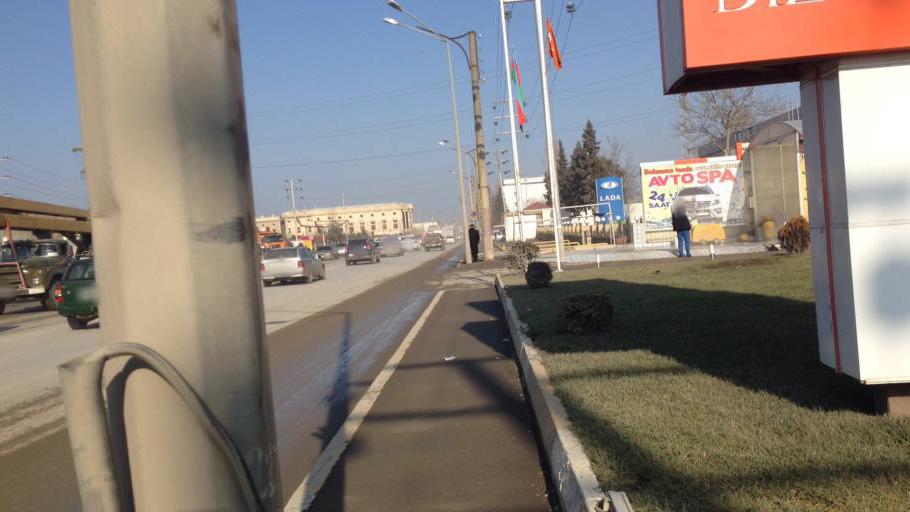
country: AZ
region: Baki
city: Binagadi
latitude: 40.4417
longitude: 49.8449
